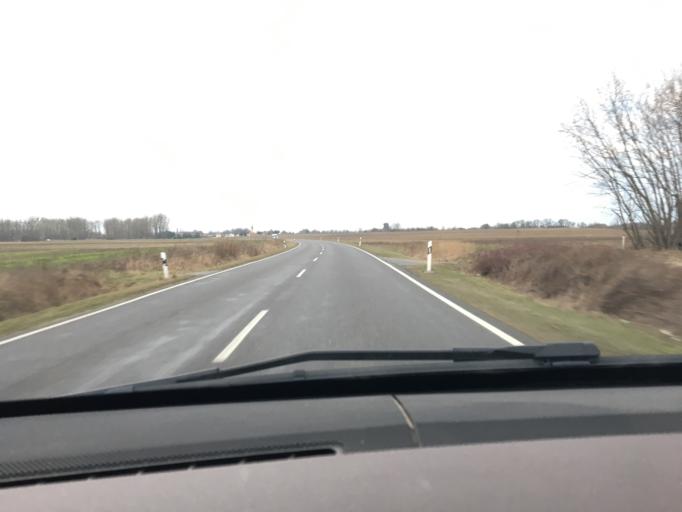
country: DE
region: Brandenburg
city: Liebenwalde
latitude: 52.8786
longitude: 13.4640
